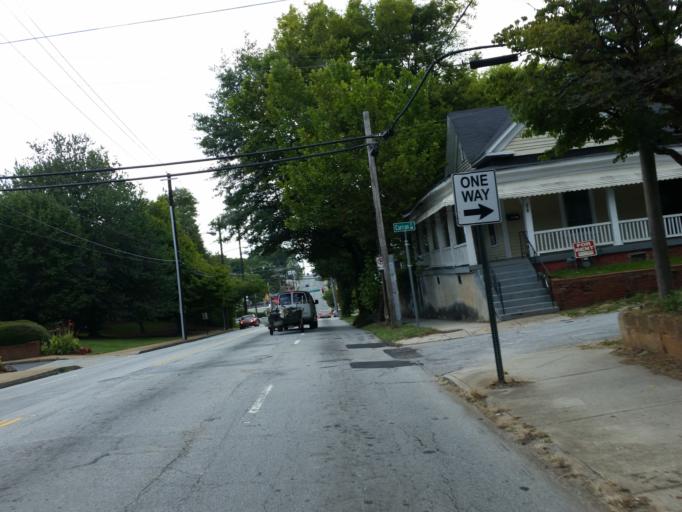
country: US
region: Georgia
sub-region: Fulton County
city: Atlanta
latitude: 33.7816
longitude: -84.4060
